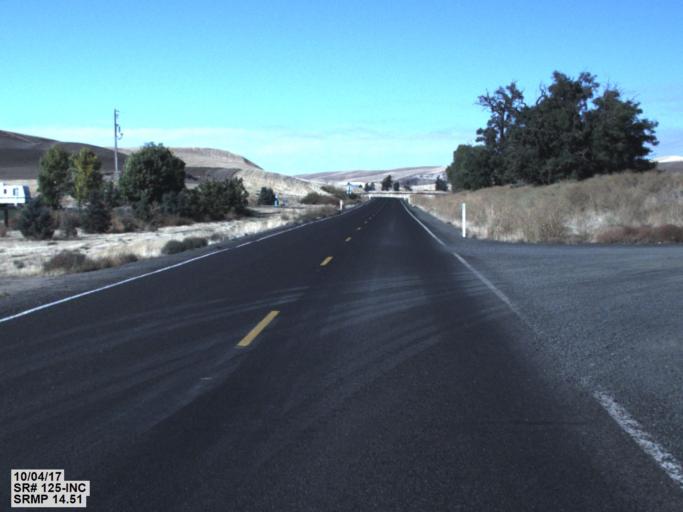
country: US
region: Washington
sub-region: Walla Walla County
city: Walla Walla
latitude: 46.1788
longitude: -118.3840
